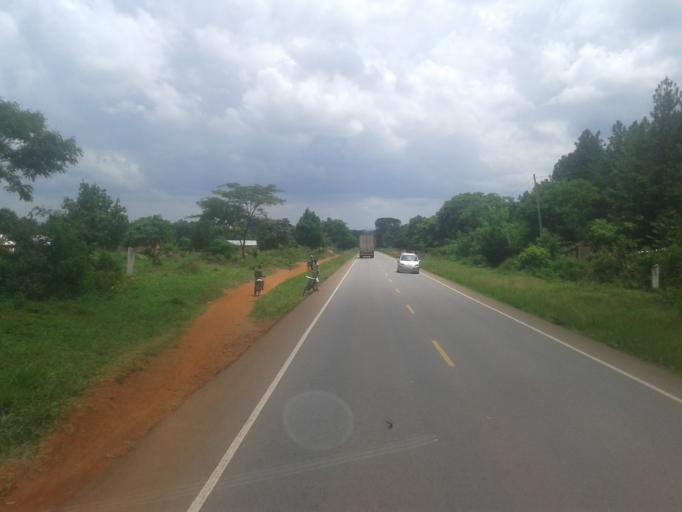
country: UG
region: Central Region
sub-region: Nakasongola District
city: Nakasongola
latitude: 1.1925
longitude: 32.4616
